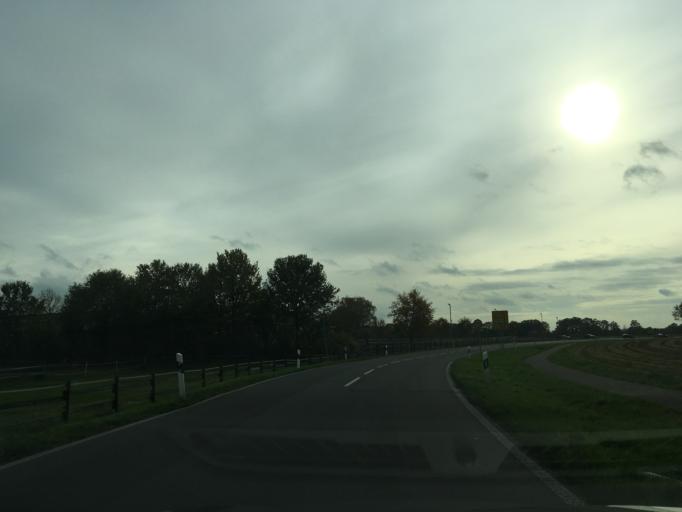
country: DE
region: North Rhine-Westphalia
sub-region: Regierungsbezirk Munster
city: Vreden
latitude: 52.0455
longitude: 6.8583
